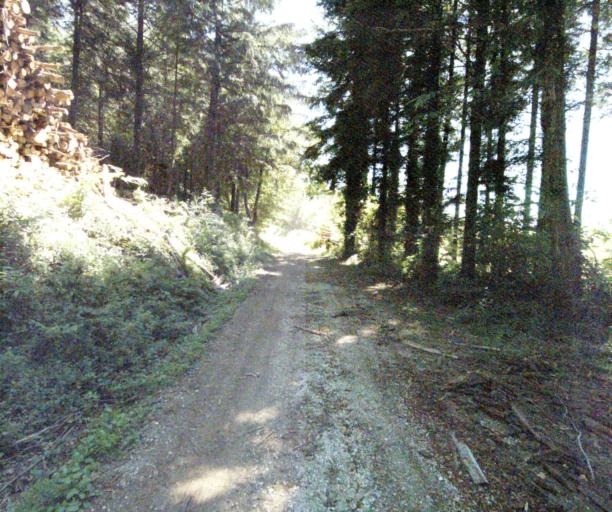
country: FR
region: Midi-Pyrenees
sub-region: Departement du Tarn
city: Soreze
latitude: 43.4434
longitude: 2.1077
